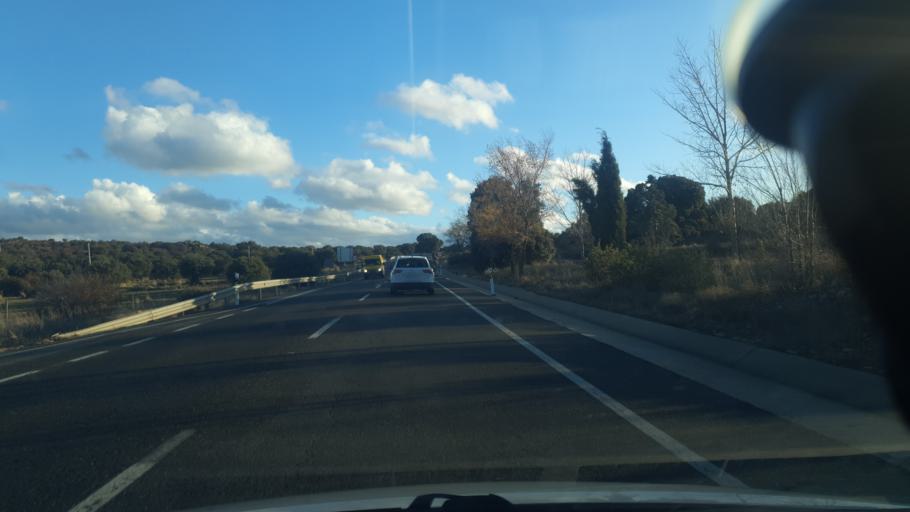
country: ES
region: Castille and Leon
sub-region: Provincia de Avila
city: Mingorria
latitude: 40.7234
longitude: -4.6741
